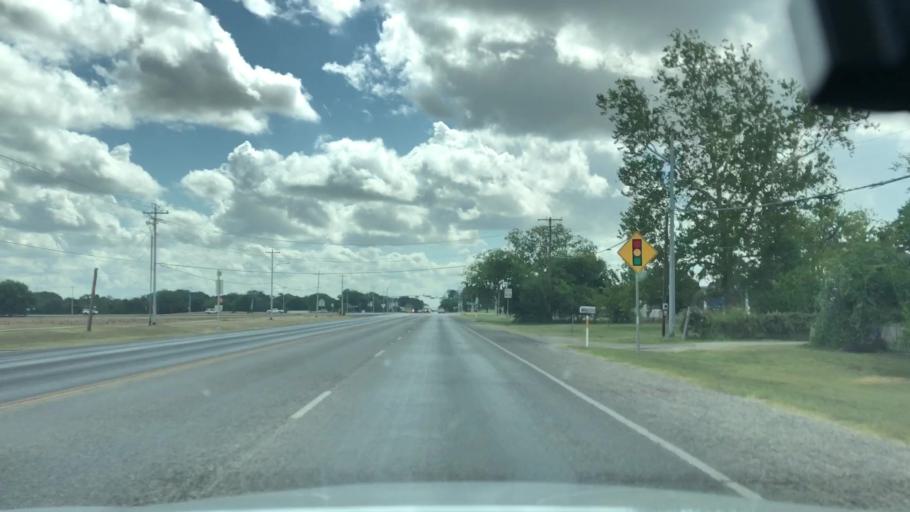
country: US
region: Texas
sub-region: Guadalupe County
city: Seguin
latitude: 29.5692
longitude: -97.9920
